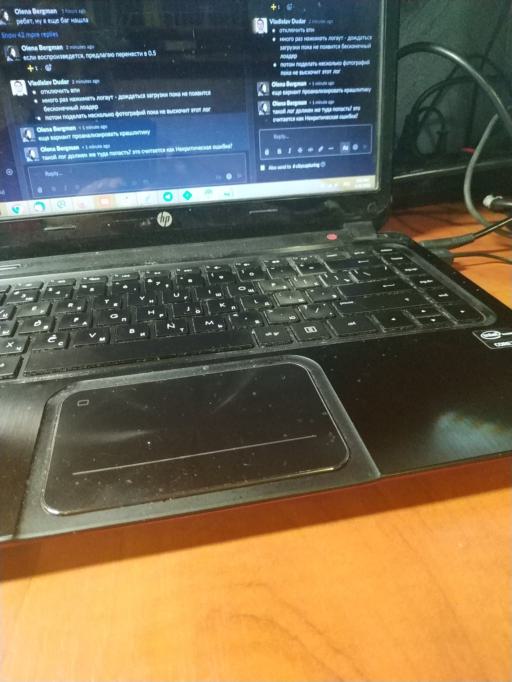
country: RU
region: Tverskaya
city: Likhoslavl'
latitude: 57.1364
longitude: 35.4506
